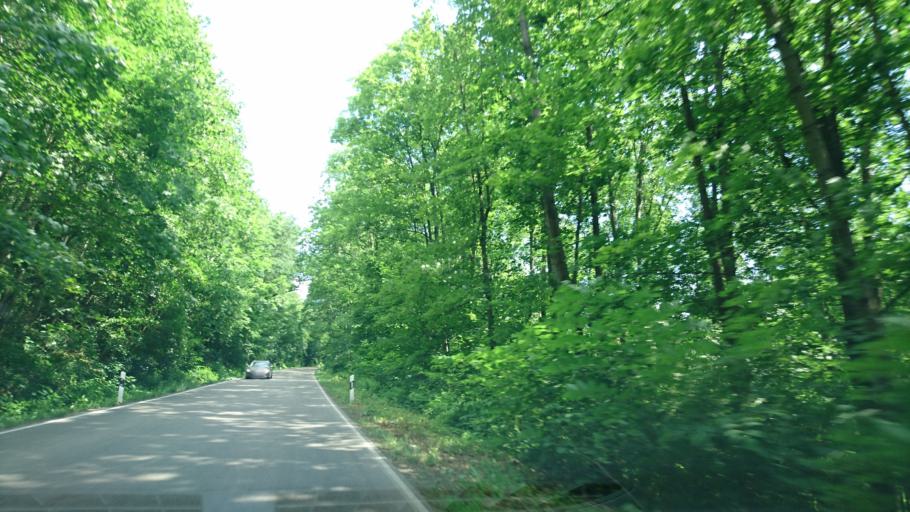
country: DE
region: Saxony
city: Struppen
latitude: 50.9222
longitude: 13.9759
